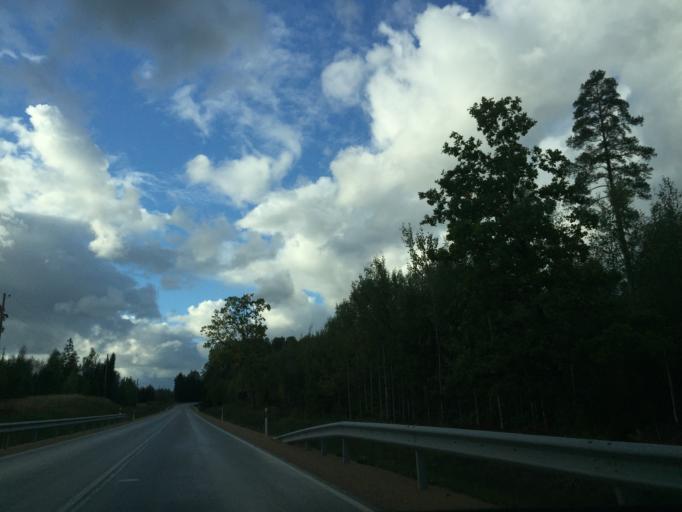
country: LV
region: Ligatne
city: Ligatne
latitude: 57.1623
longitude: 25.0545
